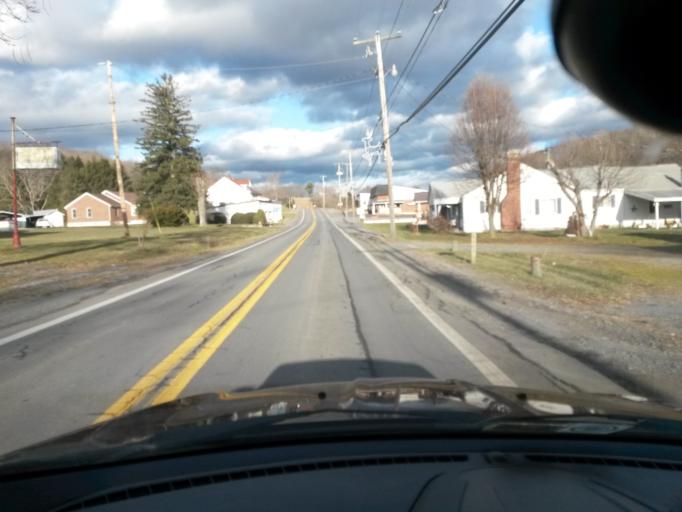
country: US
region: Virginia
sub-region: Giles County
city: Pembroke
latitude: 37.4531
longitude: -80.6705
